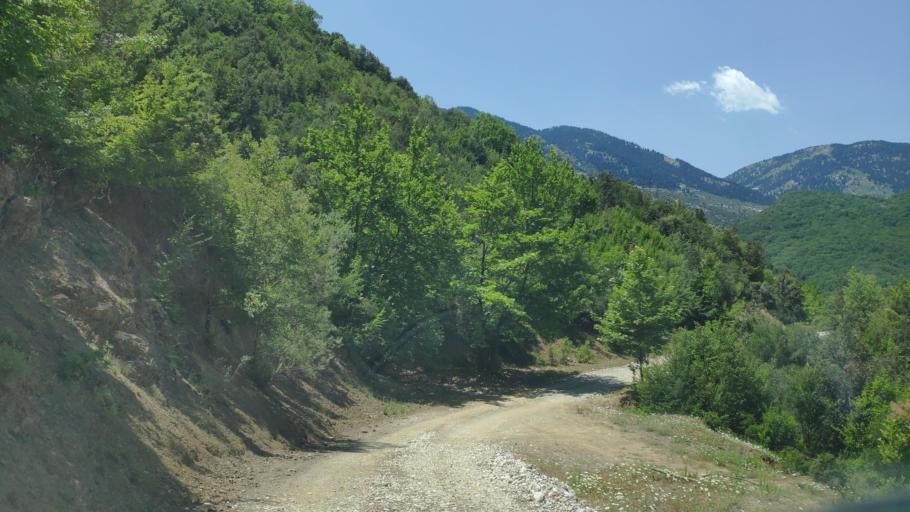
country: GR
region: Thessaly
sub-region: Nomos Kardhitsas
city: Anthiro
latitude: 39.1786
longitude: 21.3680
